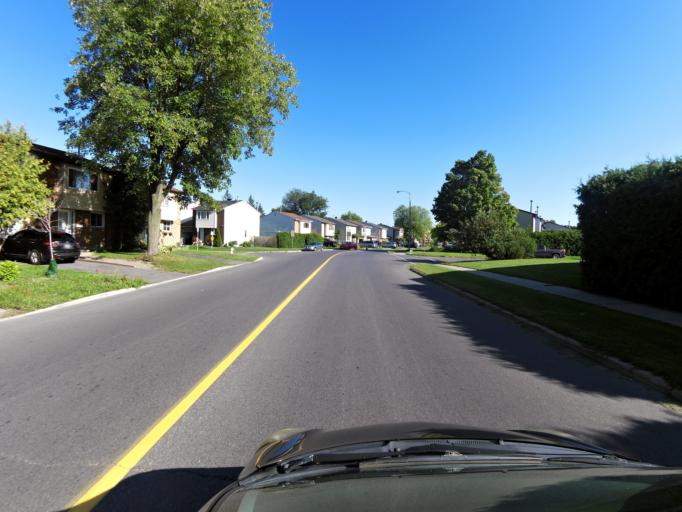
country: CA
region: Quebec
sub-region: Outaouais
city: Gatineau
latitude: 45.4653
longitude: -75.4953
